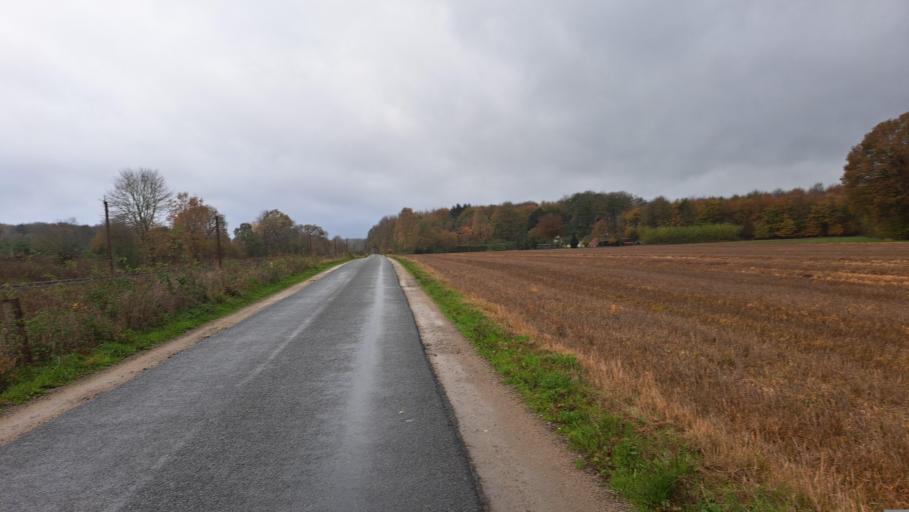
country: DK
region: Central Jutland
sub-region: Hedensted Kommune
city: Hedensted
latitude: 55.8208
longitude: 9.7199
